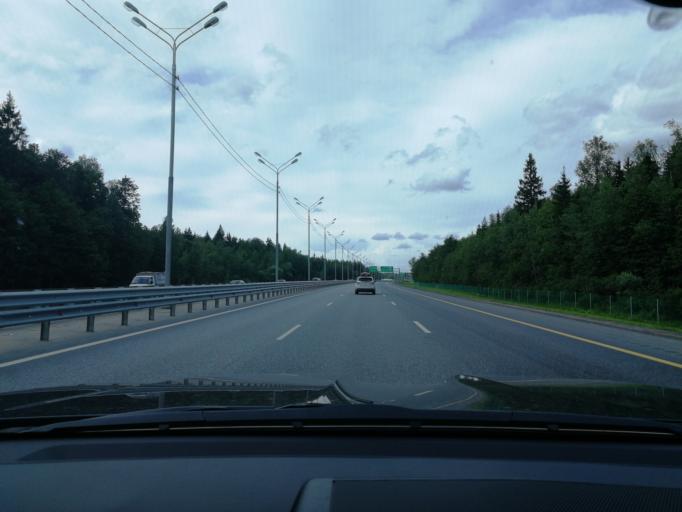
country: RU
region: Moskovskaya
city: Danki
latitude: 54.9676
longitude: 37.5296
